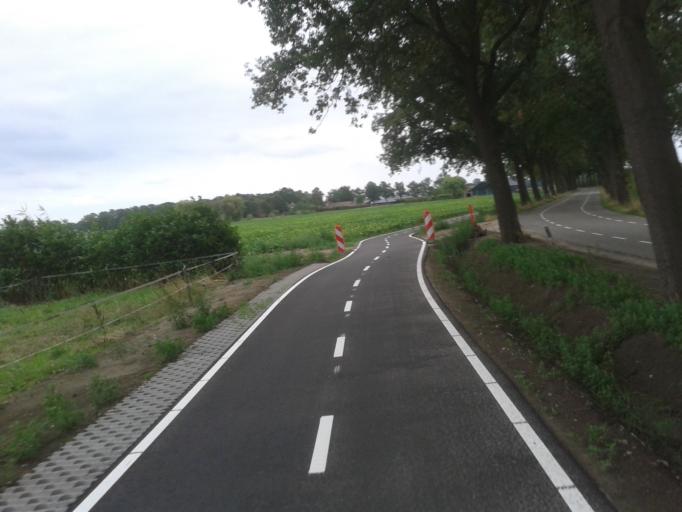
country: NL
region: North Brabant
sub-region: Gemeente Hilvarenbeek
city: Hilvarenbeek
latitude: 51.5120
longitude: 5.1959
